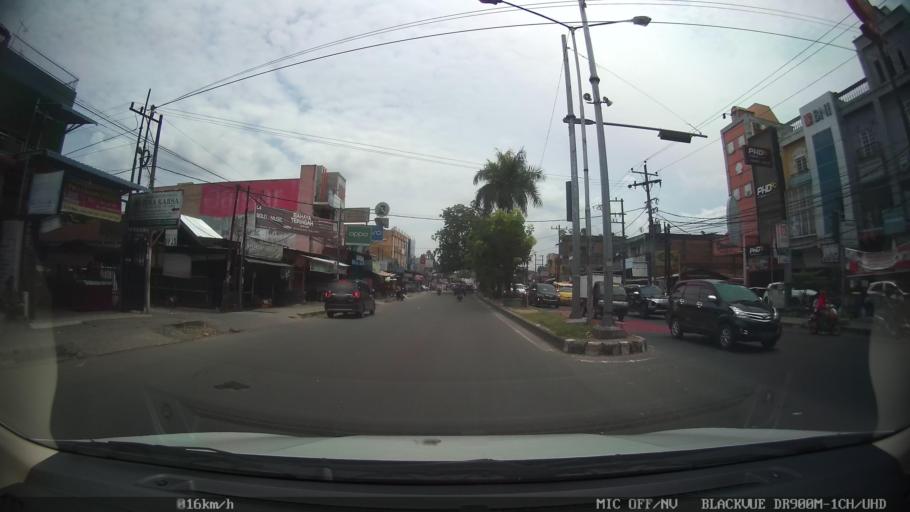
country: ID
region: North Sumatra
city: Sunggal
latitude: 3.5263
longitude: 98.6330
